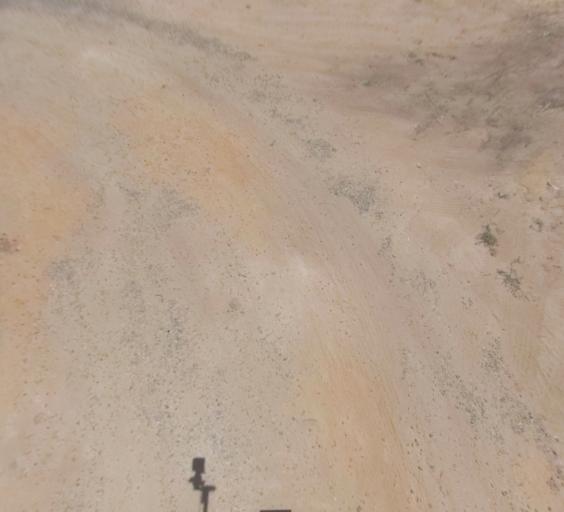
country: US
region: California
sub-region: Madera County
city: Madera
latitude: 36.9801
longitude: -120.0420
